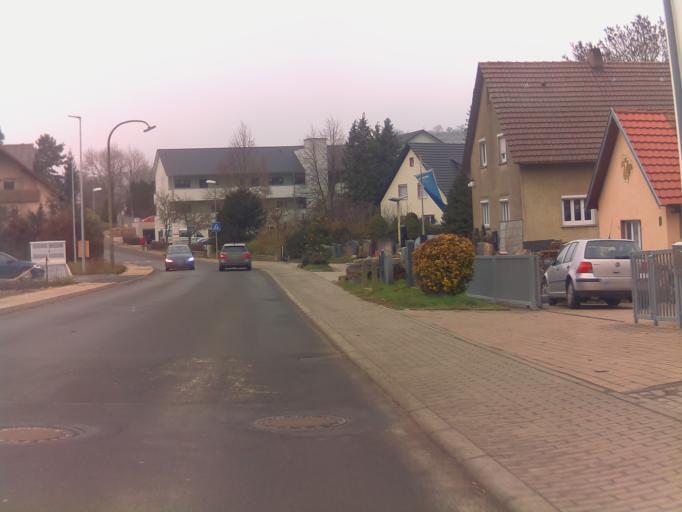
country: DE
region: Baden-Wuerttemberg
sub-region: Regierungsbezirk Stuttgart
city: Boxberg
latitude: 49.4794
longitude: 9.6381
